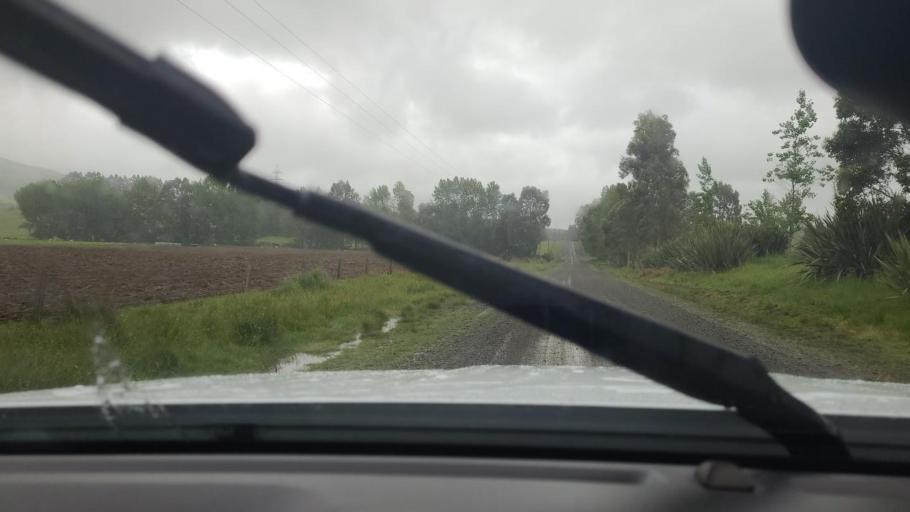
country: NZ
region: Southland
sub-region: Southland District
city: Riverton
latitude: -45.9517
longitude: 167.9200
